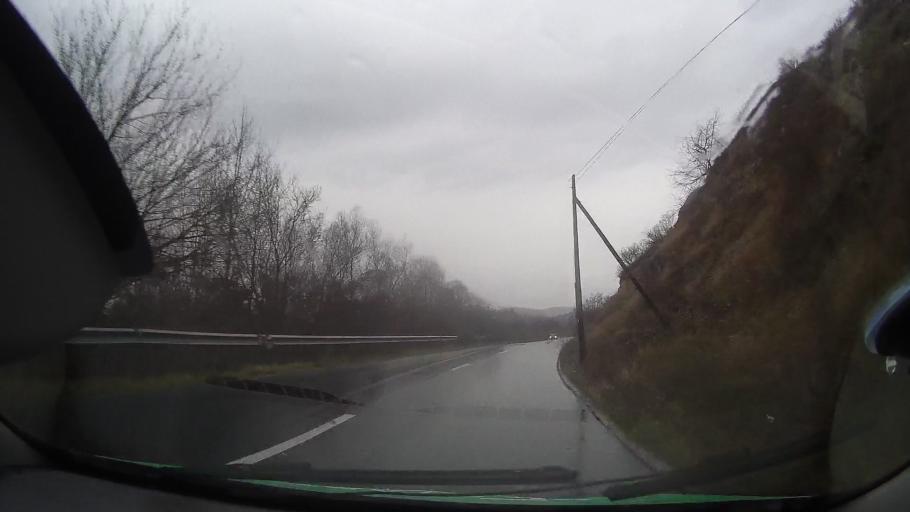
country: RO
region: Bihor
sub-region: Comuna Pocola
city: Pocola
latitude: 46.6837
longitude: 22.2598
